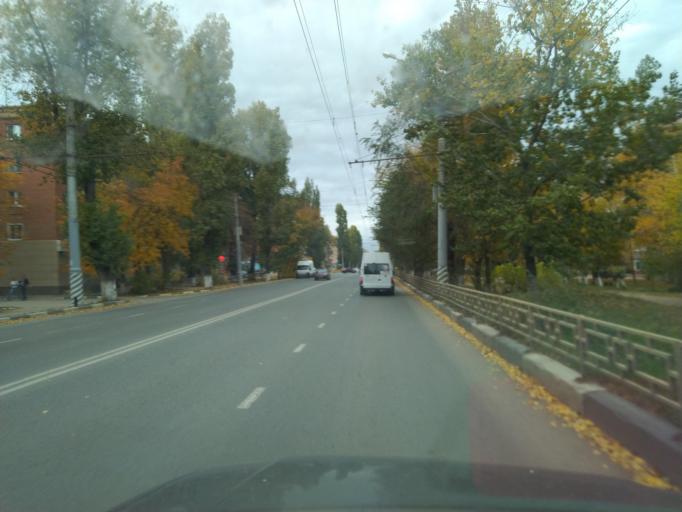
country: RU
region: Saratov
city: Engel's
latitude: 51.4763
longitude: 46.1306
